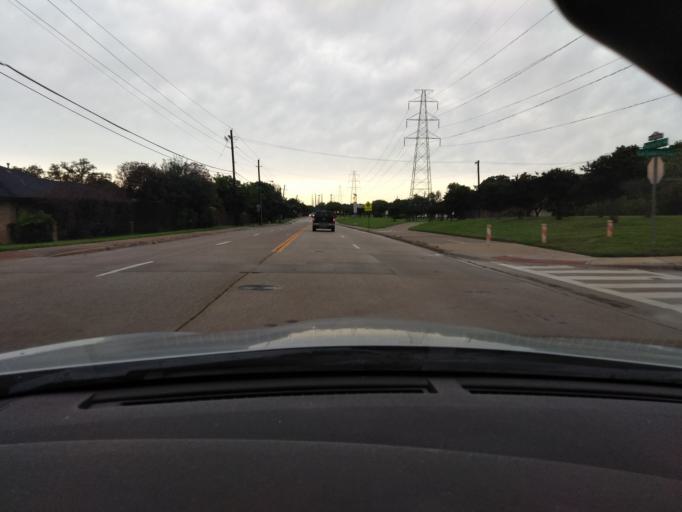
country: US
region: Texas
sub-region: Dallas County
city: Addison
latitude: 32.9686
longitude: -96.7785
